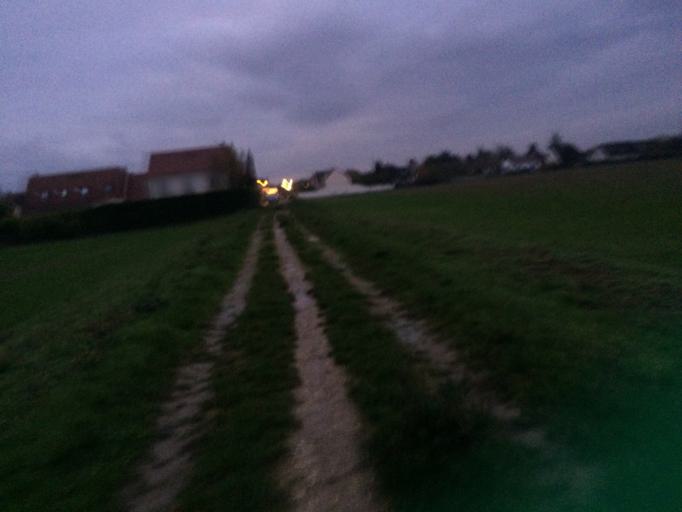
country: FR
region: Ile-de-France
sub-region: Departement de l'Essonne
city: Nozay
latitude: 48.6585
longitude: 2.2474
